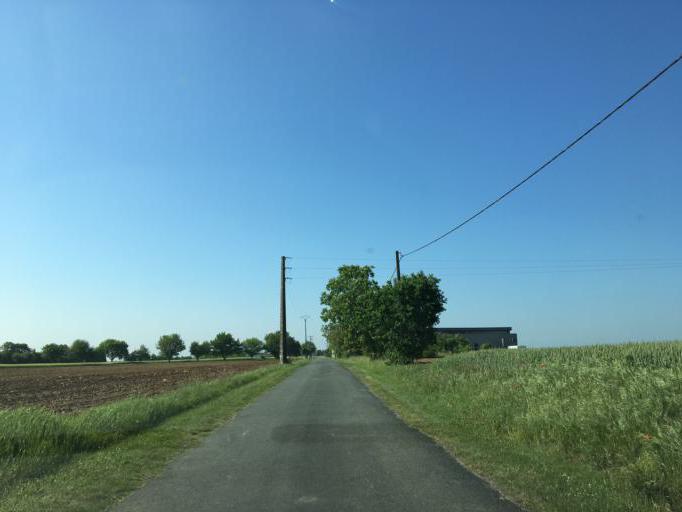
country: FR
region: Poitou-Charentes
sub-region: Departement des Deux-Sevres
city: Beauvoir-sur-Niort
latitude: 46.0918
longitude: -0.5058
